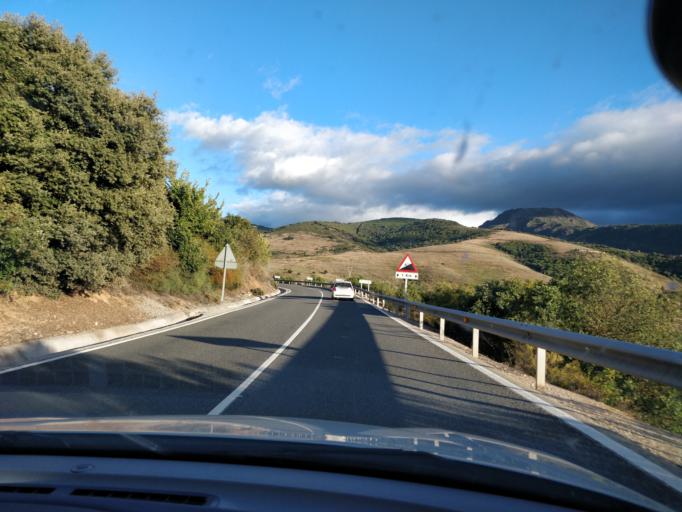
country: ES
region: Castille and Leon
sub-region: Provincia de Leon
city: Borrenes
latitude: 42.4941
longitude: -6.7163
